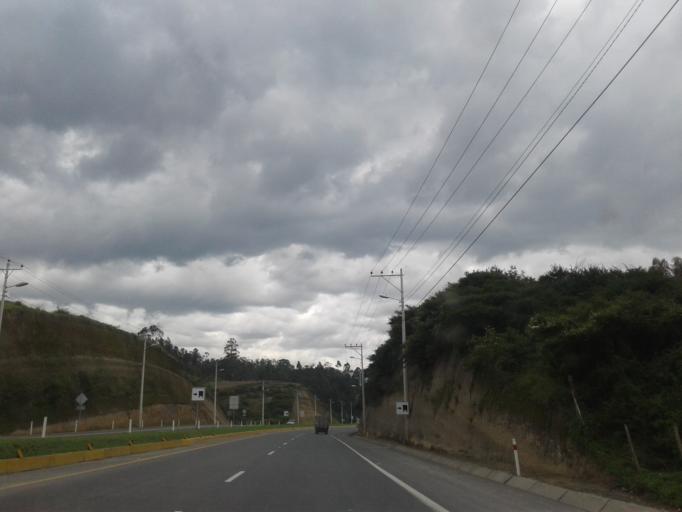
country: EC
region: Pichincha
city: Sangolqui
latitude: -0.3144
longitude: -78.3667
